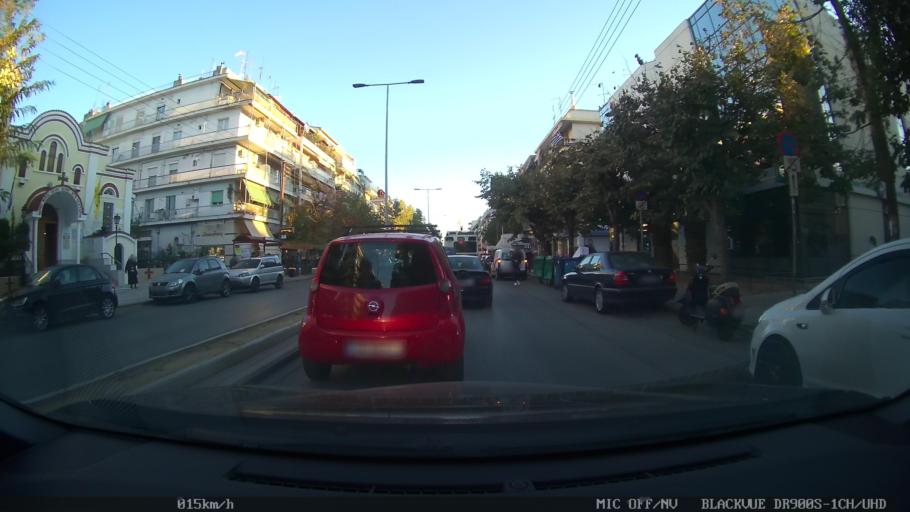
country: GR
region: Central Macedonia
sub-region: Nomos Thessalonikis
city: Triandria
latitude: 40.6042
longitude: 22.9687
